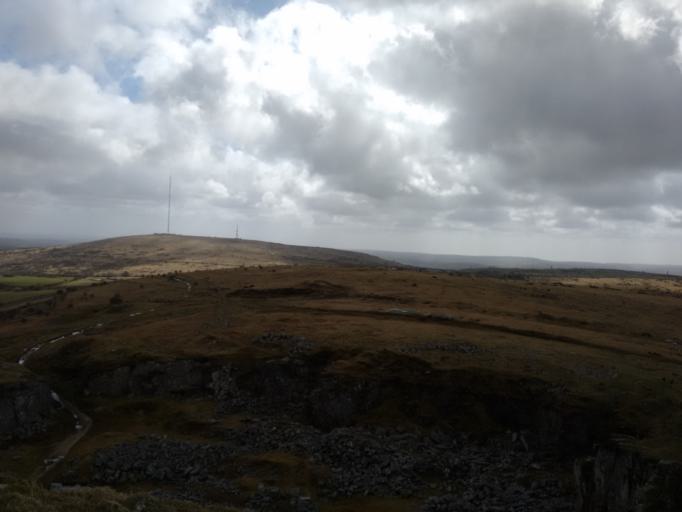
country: GB
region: England
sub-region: Cornwall
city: North Hill
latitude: 50.5255
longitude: -4.4591
